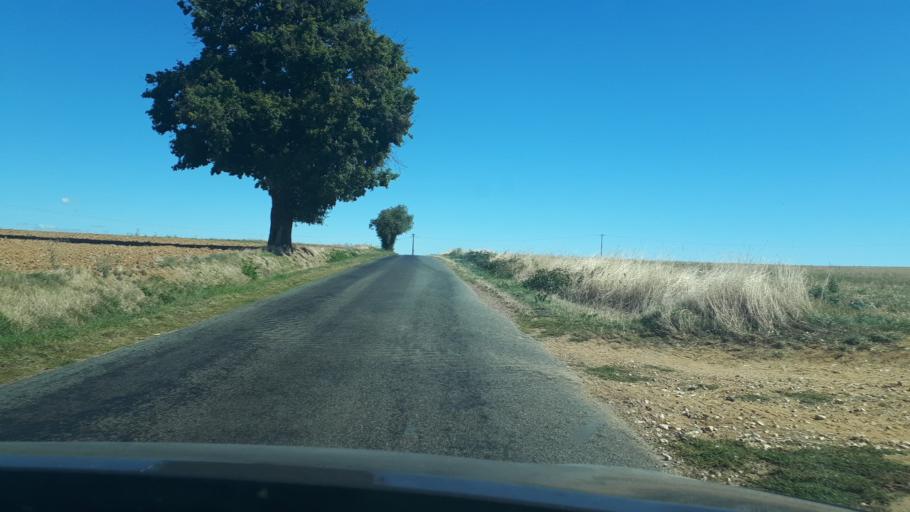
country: FR
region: Centre
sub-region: Departement du Cher
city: Sancerre
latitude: 47.3234
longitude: 2.7745
